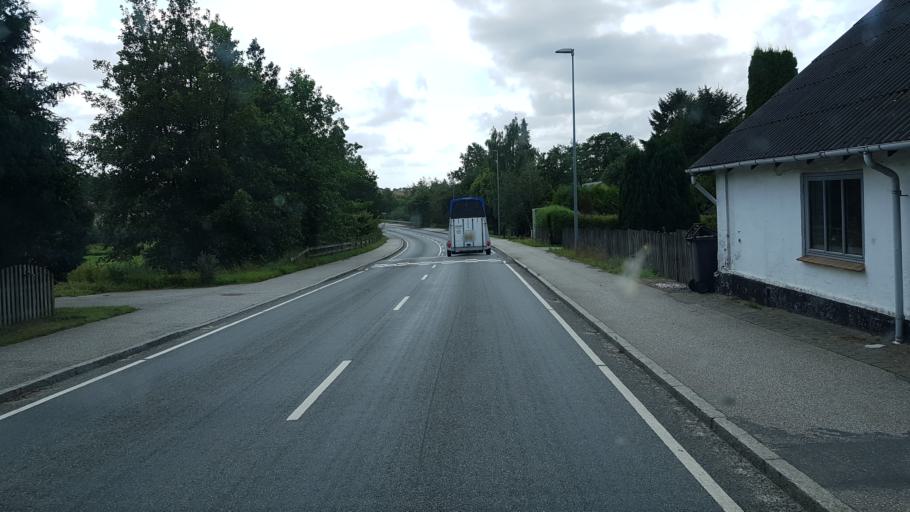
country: DK
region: South Denmark
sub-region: Vejen Kommune
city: Brorup
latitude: 55.5150
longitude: 9.0242
